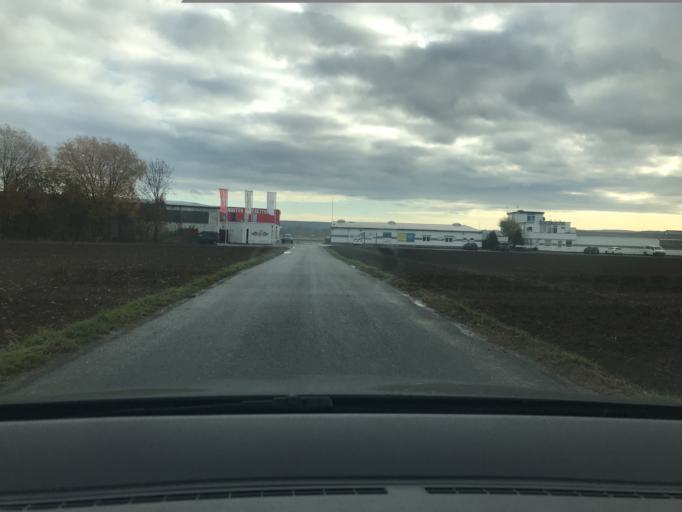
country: DE
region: Hesse
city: Reichelsheim
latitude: 50.3368
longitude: 8.8749
